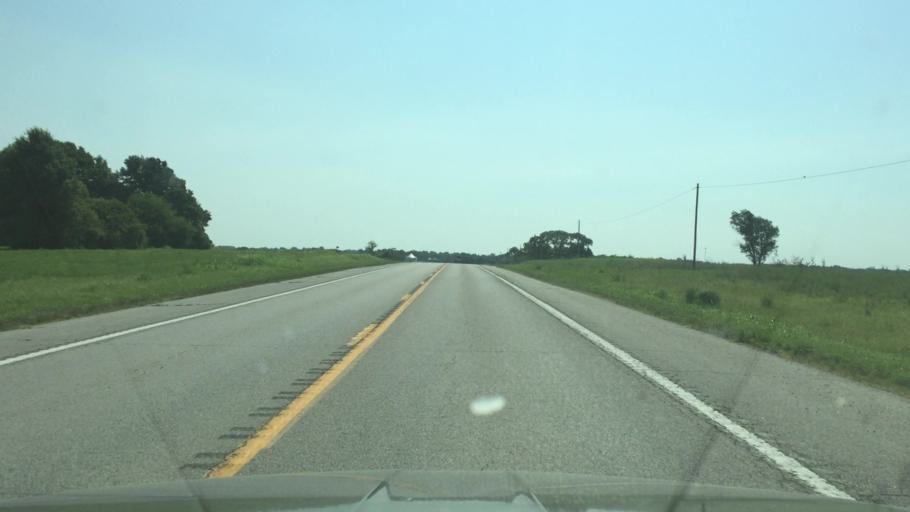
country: US
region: Missouri
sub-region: Pettis County
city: Sedalia
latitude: 38.6917
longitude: -93.0624
